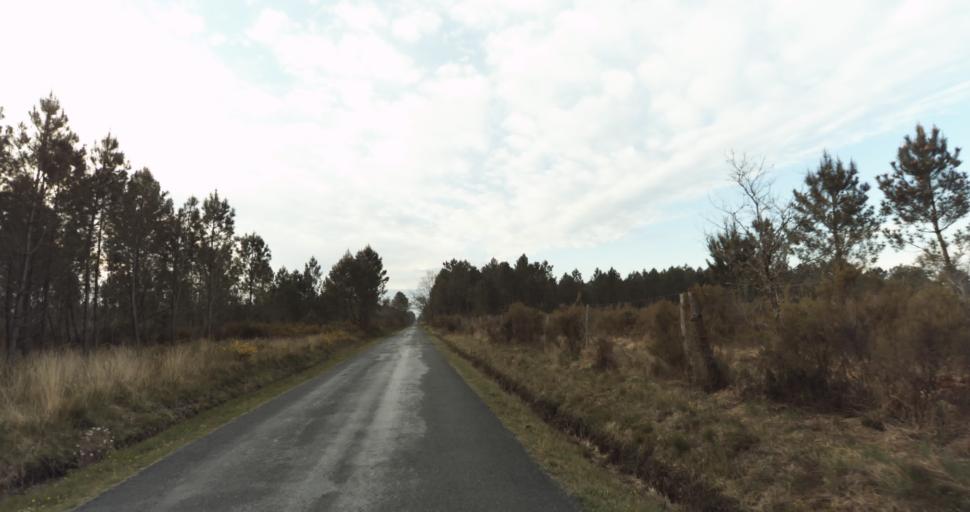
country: FR
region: Aquitaine
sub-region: Departement de la Gironde
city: Martignas-sur-Jalle
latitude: 44.7966
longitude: -0.7630
